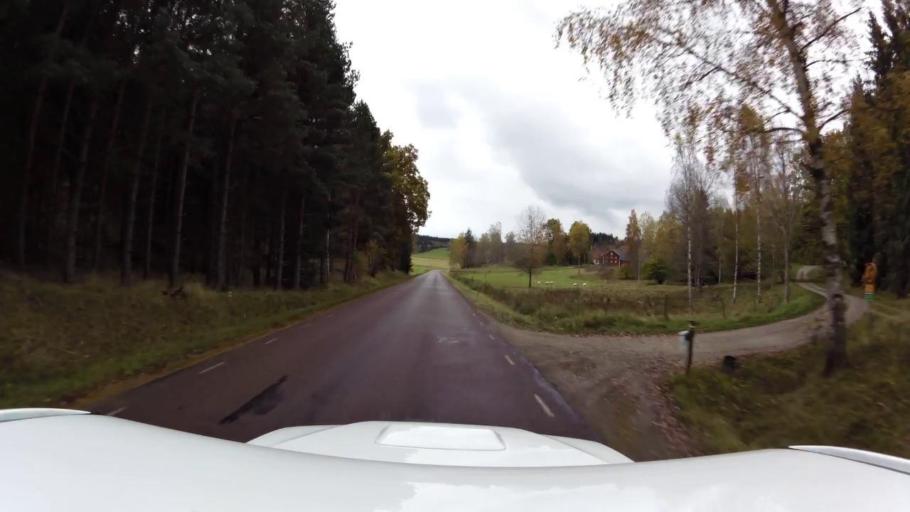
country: SE
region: OEstergoetland
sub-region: Linkopings Kommun
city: Ljungsbro
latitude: 58.5598
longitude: 15.5172
